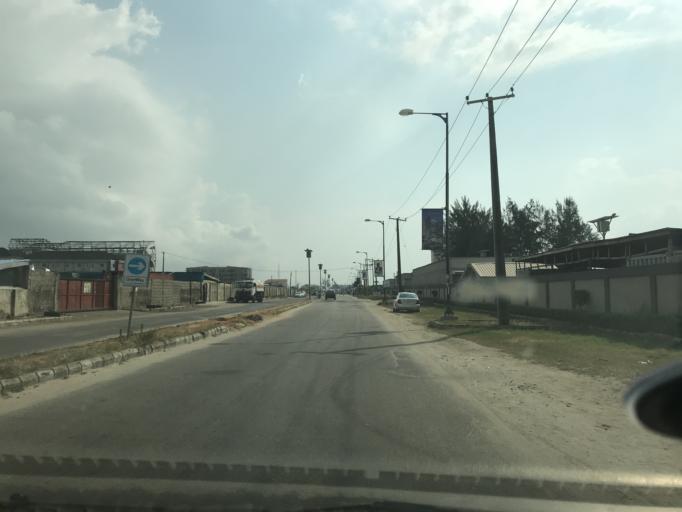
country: NG
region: Lagos
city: Ikoyi
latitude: 6.4239
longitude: 3.4441
